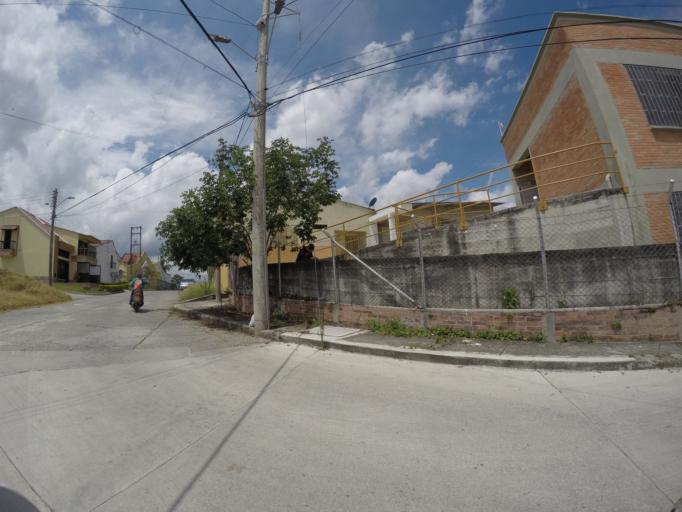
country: CO
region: Quindio
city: Quimbaya
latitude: 4.6206
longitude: -75.7694
